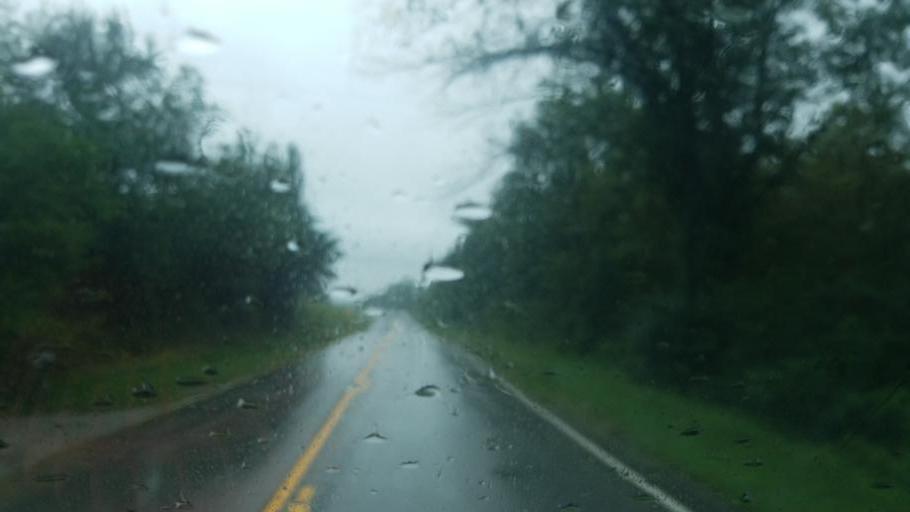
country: US
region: Kentucky
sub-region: Fleming County
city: Flemingsburg
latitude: 38.3394
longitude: -83.5974
